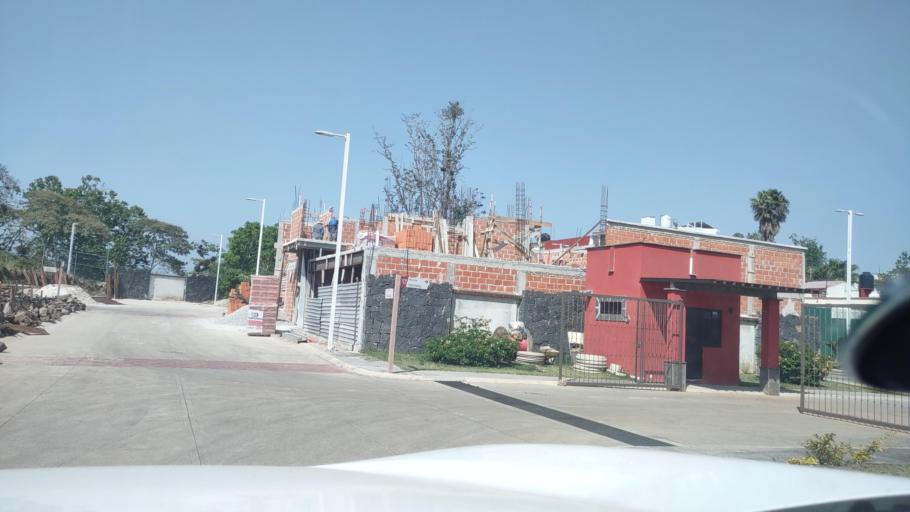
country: MX
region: Veracruz
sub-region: Emiliano Zapata
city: Las Trancas
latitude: 19.5242
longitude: -96.8697
